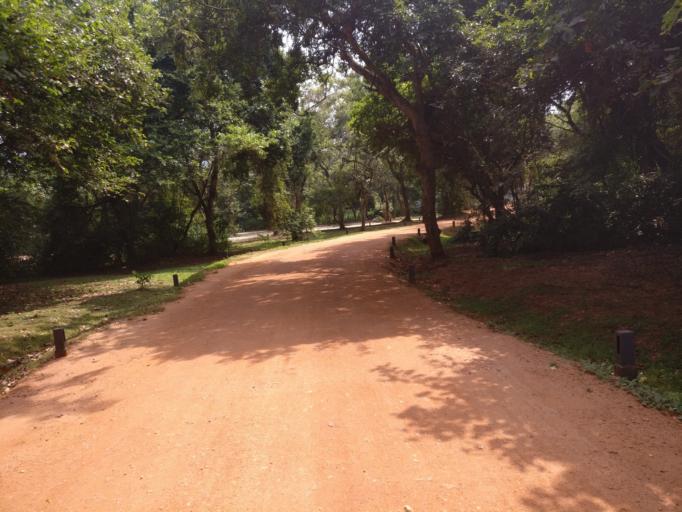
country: LK
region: Central
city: Dambulla
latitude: 7.8405
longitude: 80.6474
